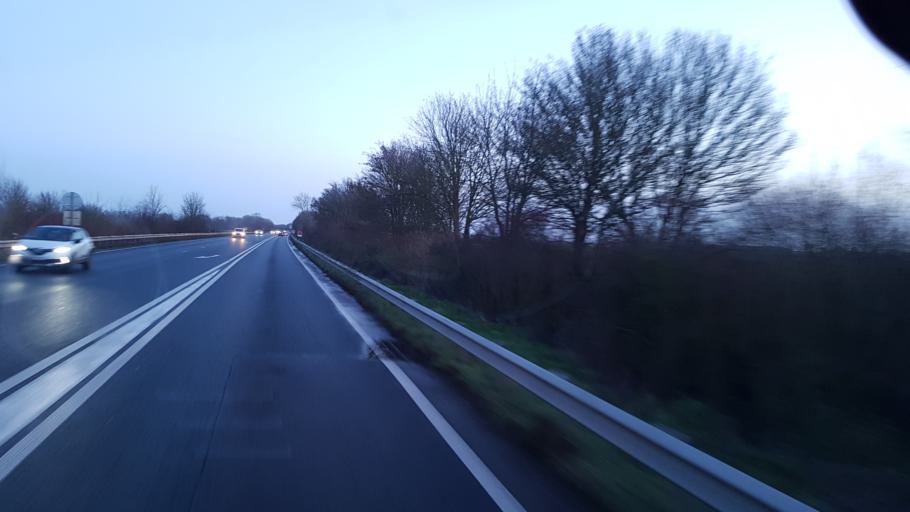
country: FR
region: Nord-Pas-de-Calais
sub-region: Departement du Nord
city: Lambres-lez-Douai
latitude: 50.3419
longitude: 3.0792
